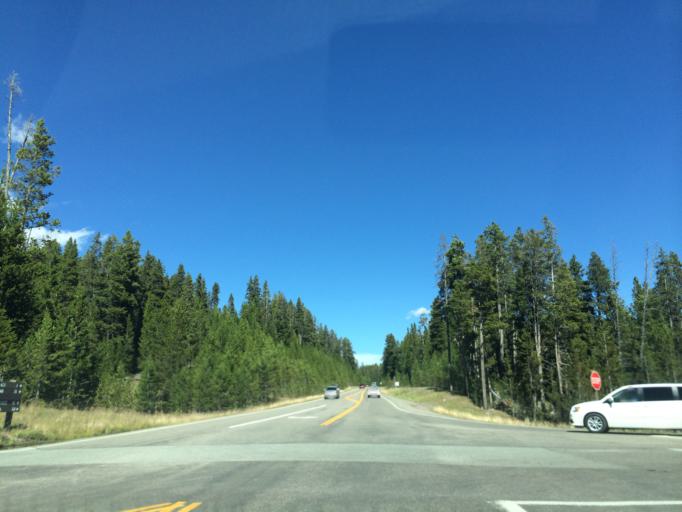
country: US
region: Montana
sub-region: Gallatin County
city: West Yellowstone
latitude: 44.5679
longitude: -110.3885
